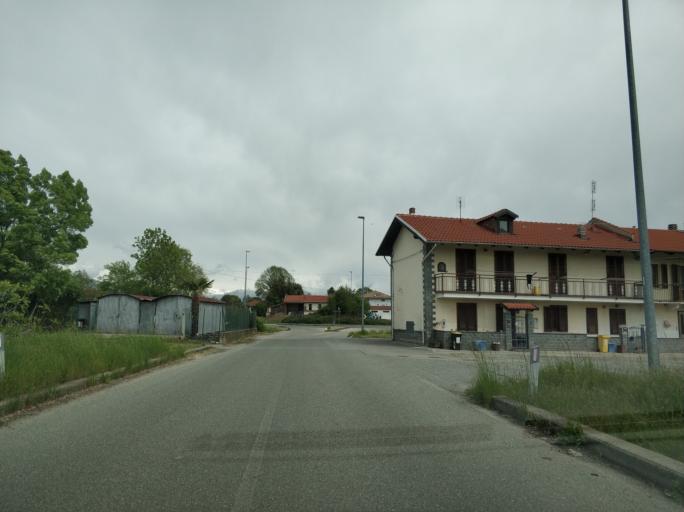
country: IT
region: Piedmont
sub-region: Provincia di Torino
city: Caselle Torinese
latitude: 45.1675
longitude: 7.6491
